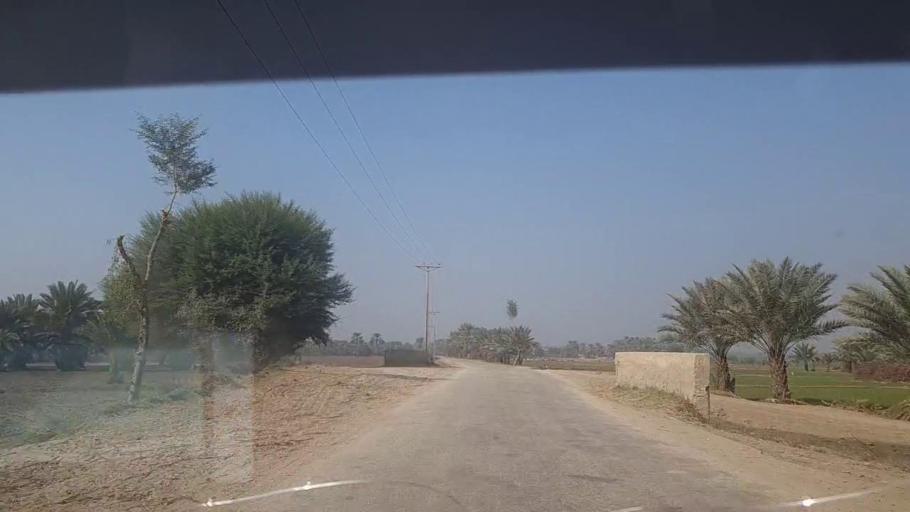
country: PK
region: Sindh
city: Kot Diji
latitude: 27.3735
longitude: 68.6976
